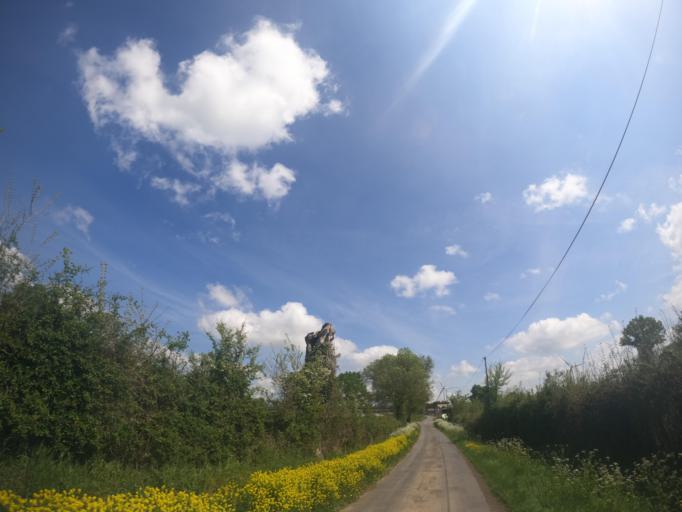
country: FR
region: Poitou-Charentes
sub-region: Departement des Deux-Sevres
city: Saint-Varent
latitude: 46.8637
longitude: -0.2363
